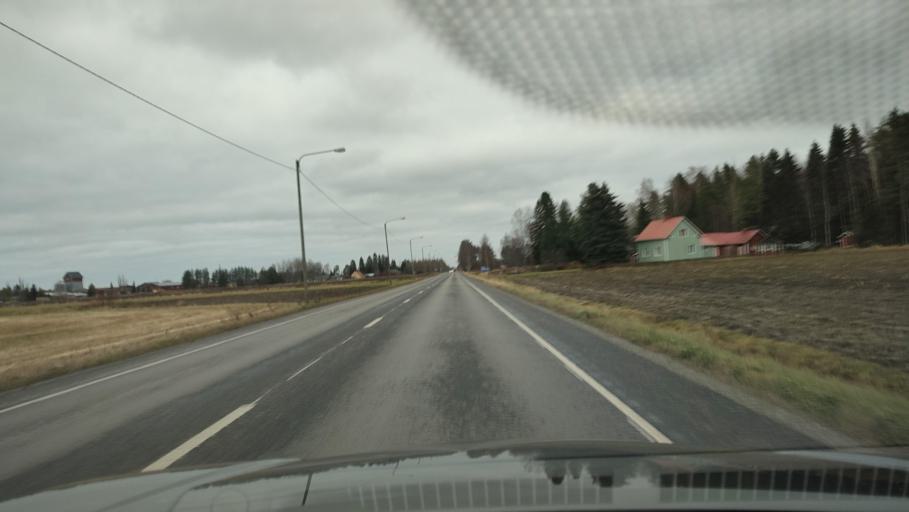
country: FI
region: Southern Ostrobothnia
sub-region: Seinaejoki
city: Ilmajoki
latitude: 62.6912
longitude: 22.4945
